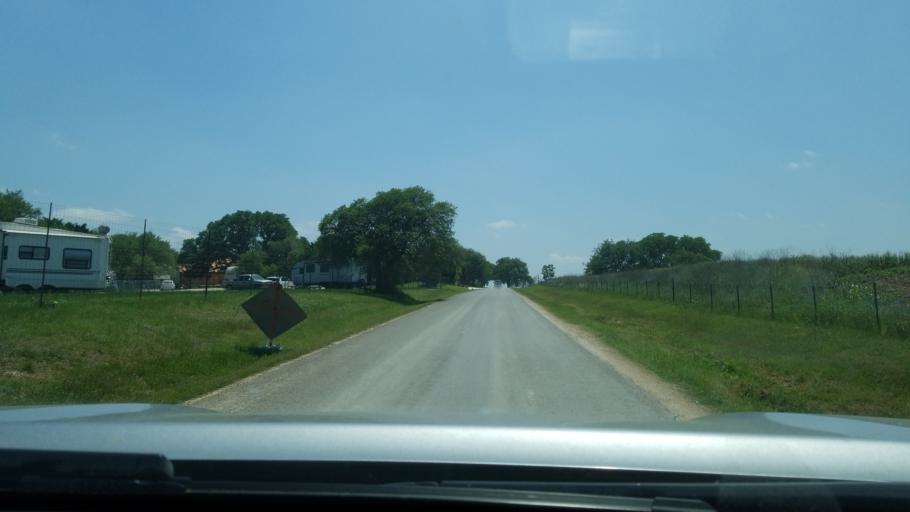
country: US
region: Texas
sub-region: Blanco County
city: Blanco
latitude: 30.0715
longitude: -98.3980
